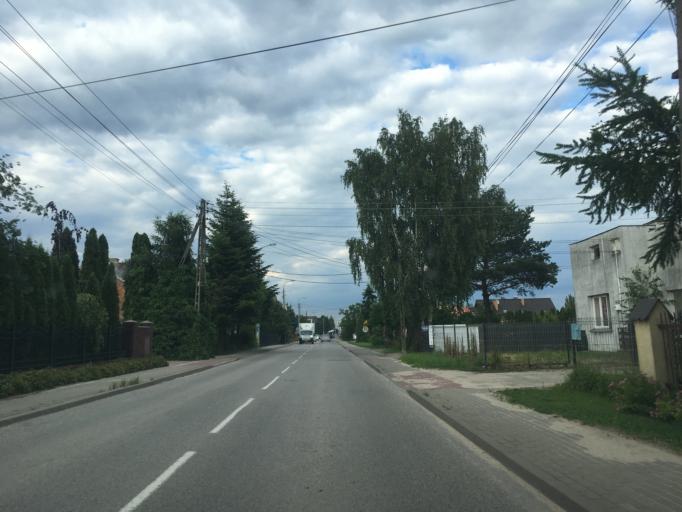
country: PL
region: Masovian Voivodeship
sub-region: Powiat piaseczynski
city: Mysiadlo
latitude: 52.1084
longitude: 20.9807
